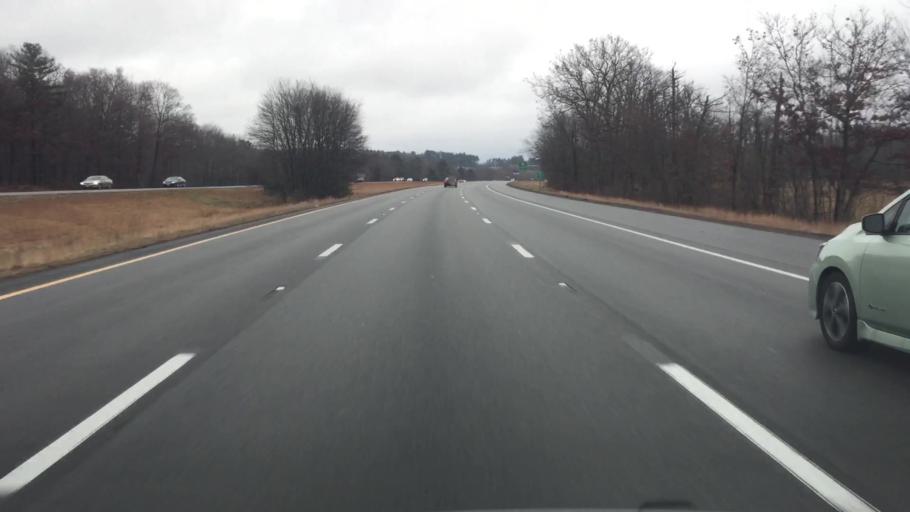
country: US
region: Massachusetts
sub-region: Norfolk County
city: Bellingham
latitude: 42.1011
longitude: -71.4416
